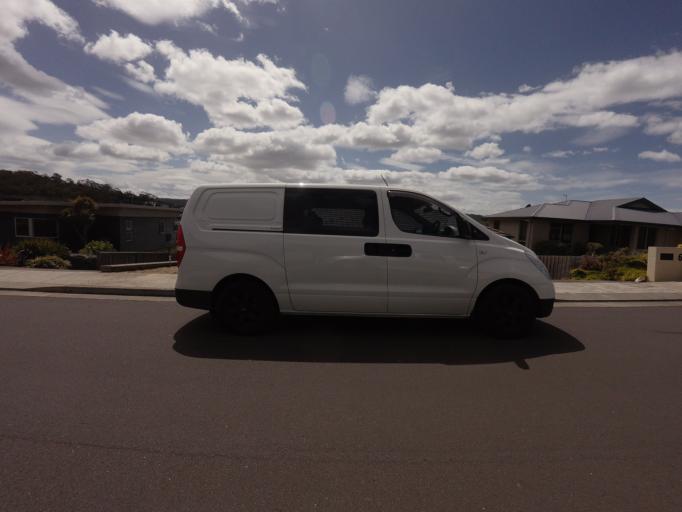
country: AU
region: Tasmania
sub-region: Clarence
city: Howrah
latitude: -42.8900
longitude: 147.4212
